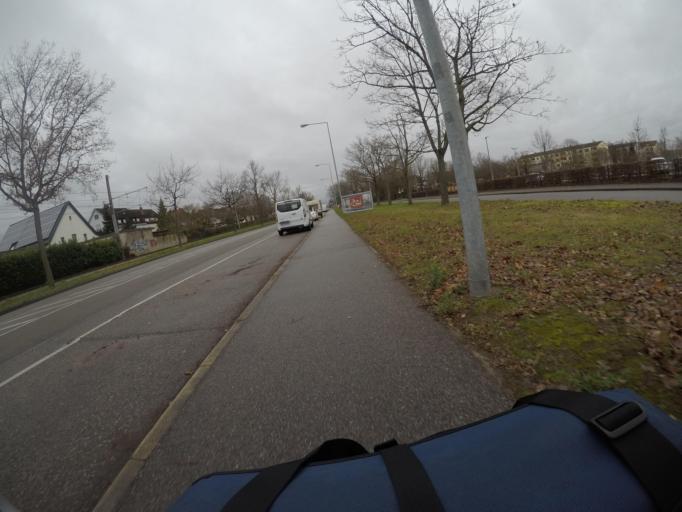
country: DE
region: Baden-Wuerttemberg
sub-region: Karlsruhe Region
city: Karlsruhe
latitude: 49.0268
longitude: 8.3451
